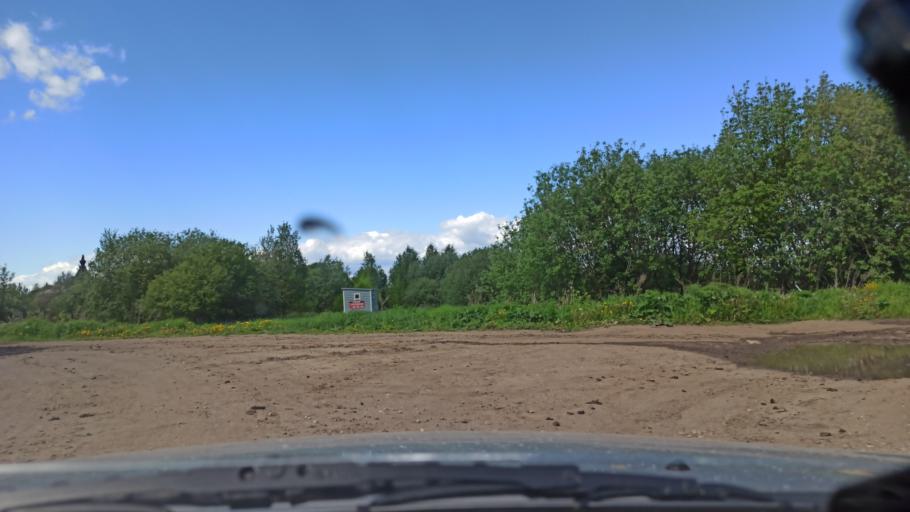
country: RU
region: Vologda
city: Vologda
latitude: 59.3409
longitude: 39.8382
